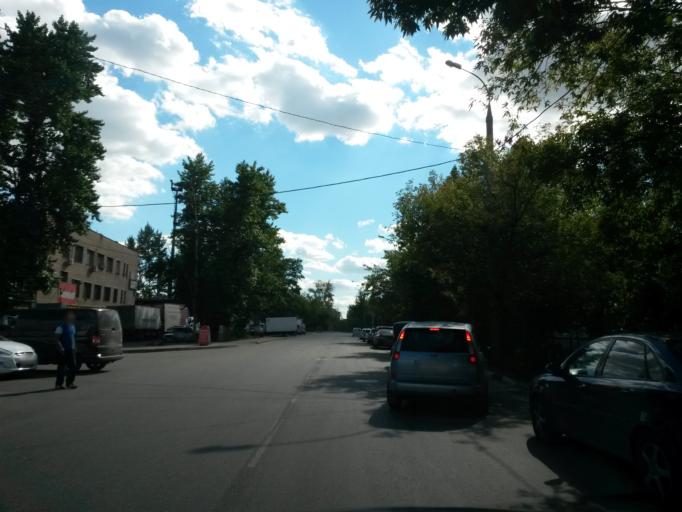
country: RU
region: Moskovskaya
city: Kozhukhovo
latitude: 55.7008
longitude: 37.6875
